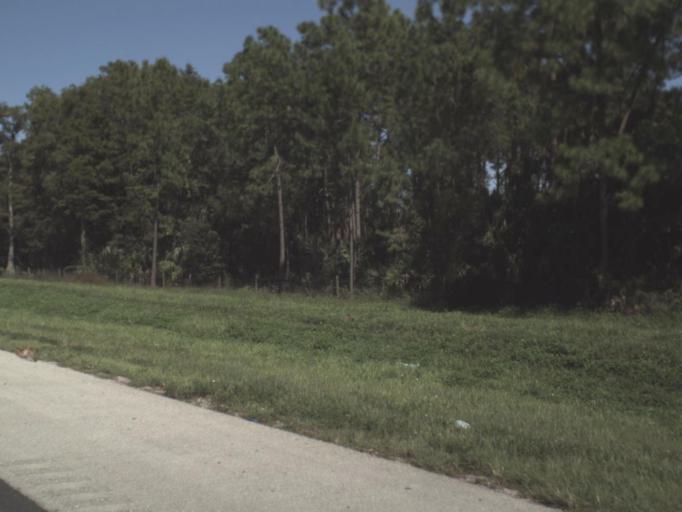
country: US
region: Florida
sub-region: Lee County
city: Bonita Springs
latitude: 26.2888
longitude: -81.7427
